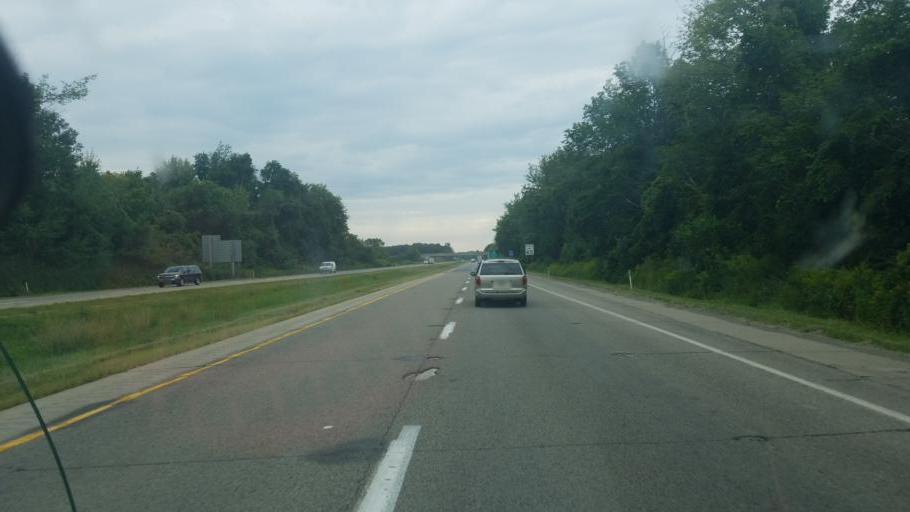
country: US
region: Pennsylvania
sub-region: Erie County
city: Fairview
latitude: 42.0174
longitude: -80.1963
